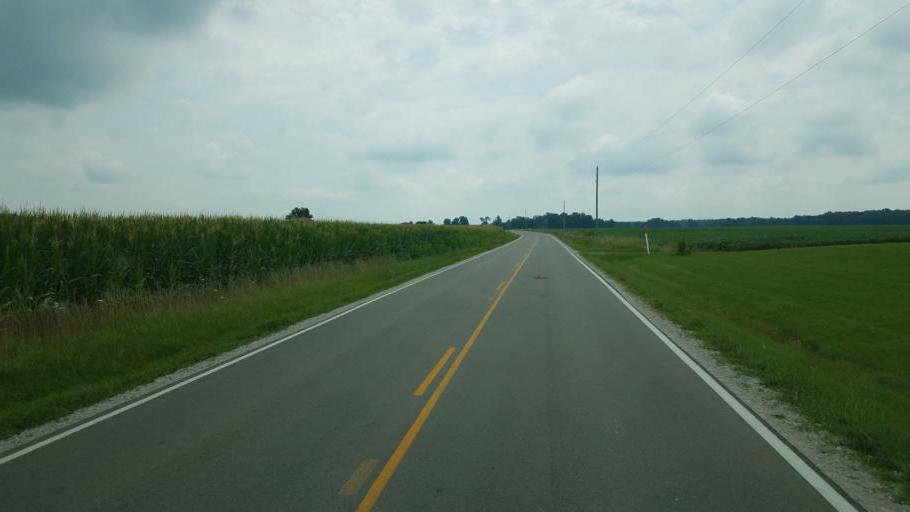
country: US
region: Ohio
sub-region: Crawford County
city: Bucyrus
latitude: 40.7179
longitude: -82.9594
